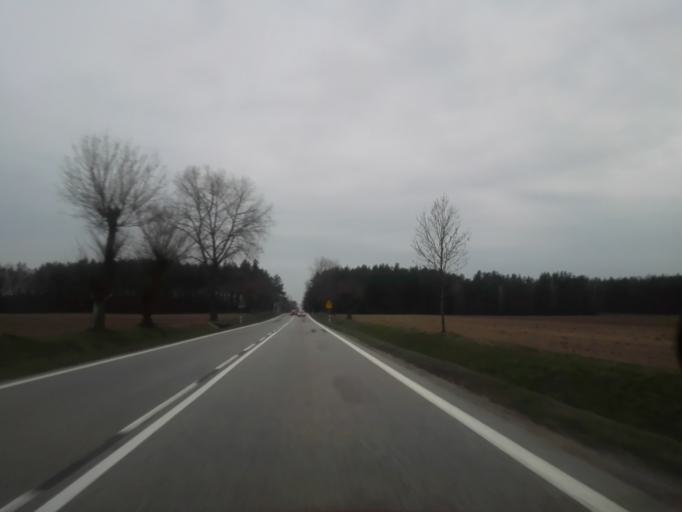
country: PL
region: Podlasie
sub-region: Powiat kolnenski
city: Stawiski
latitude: 53.2897
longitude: 22.1433
